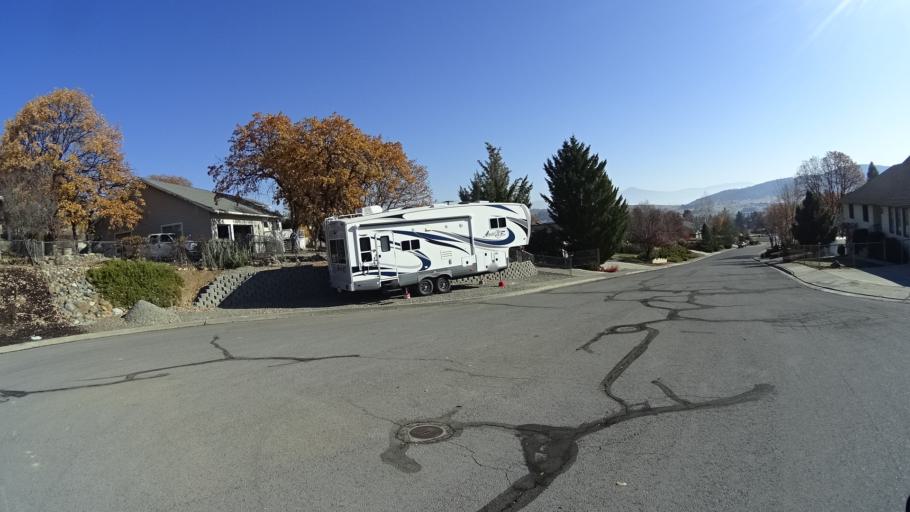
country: US
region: California
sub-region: Siskiyou County
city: Yreka
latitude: 41.7437
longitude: -122.6466
